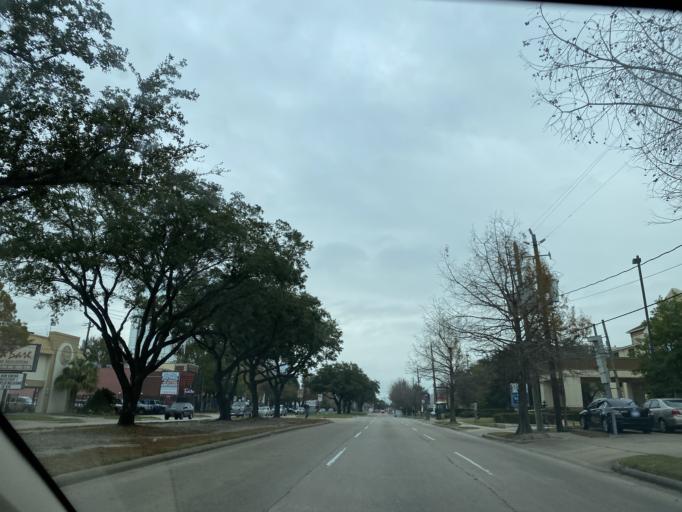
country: US
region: Texas
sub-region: Harris County
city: Piney Point Village
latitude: 29.7317
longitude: -95.4933
